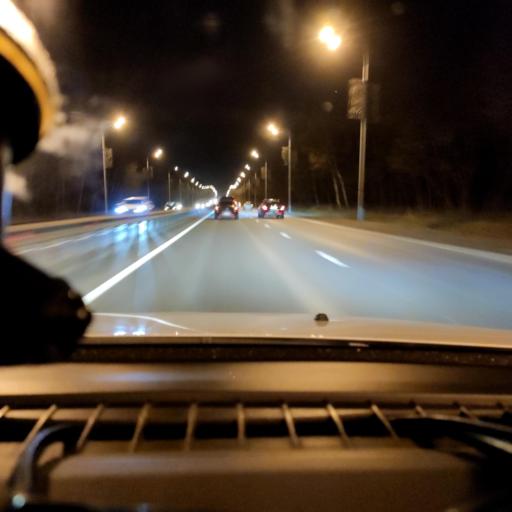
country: RU
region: Samara
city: Novosemeykino
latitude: 53.3273
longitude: 50.2311
